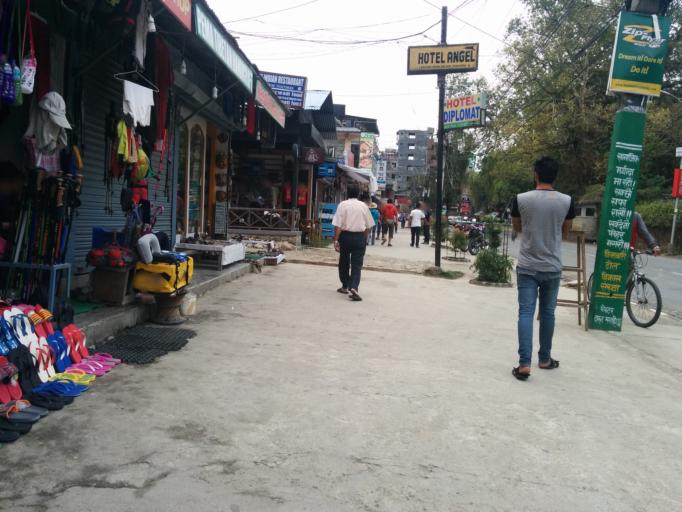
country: NP
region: Western Region
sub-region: Gandaki Zone
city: Pokhara
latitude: 28.2067
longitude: 83.9590
